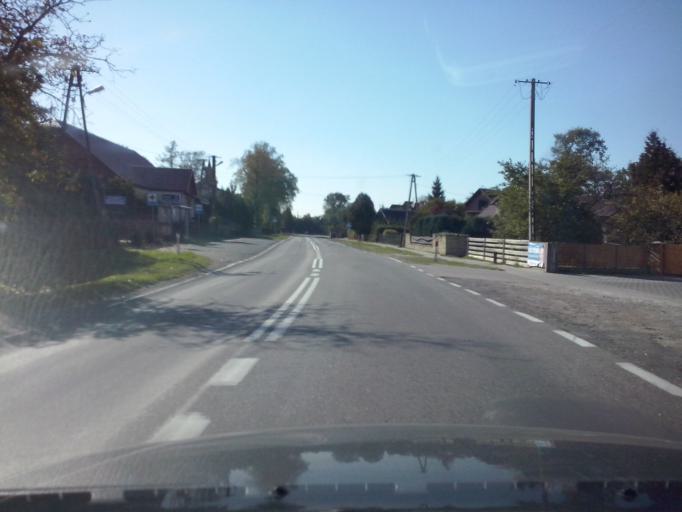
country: PL
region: Lublin Voivodeship
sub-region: Powiat bilgorajski
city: Bilgoraj
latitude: 50.5175
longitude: 22.6706
